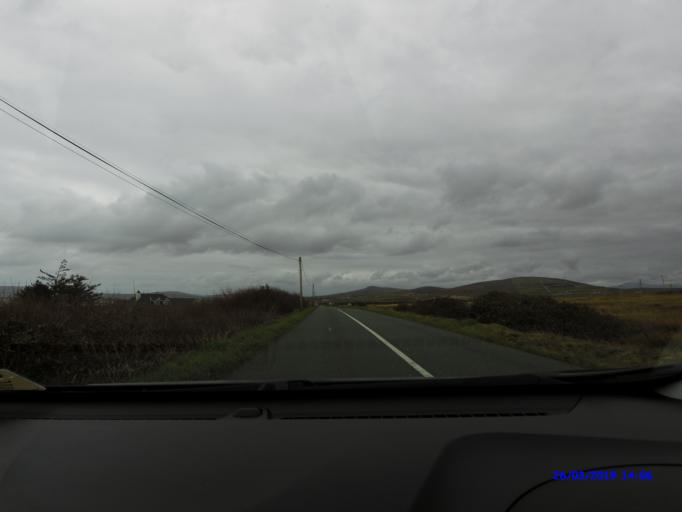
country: IE
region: Connaught
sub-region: Maigh Eo
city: Belmullet
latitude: 54.2070
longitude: -9.9298
